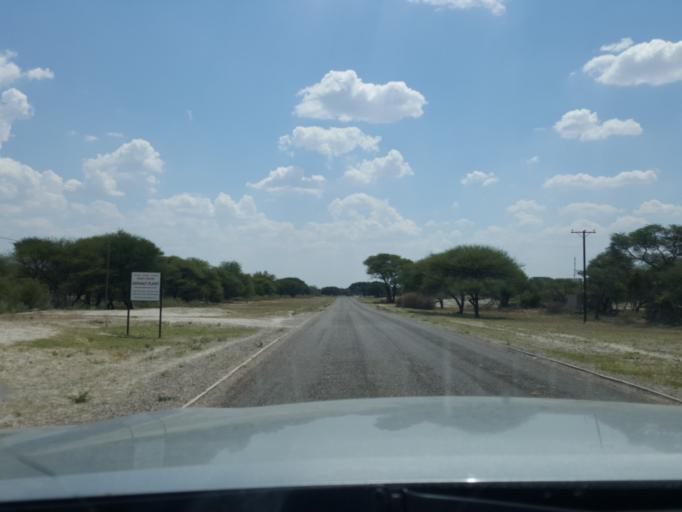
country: BW
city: Tsau
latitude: -20.1807
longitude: 22.4649
